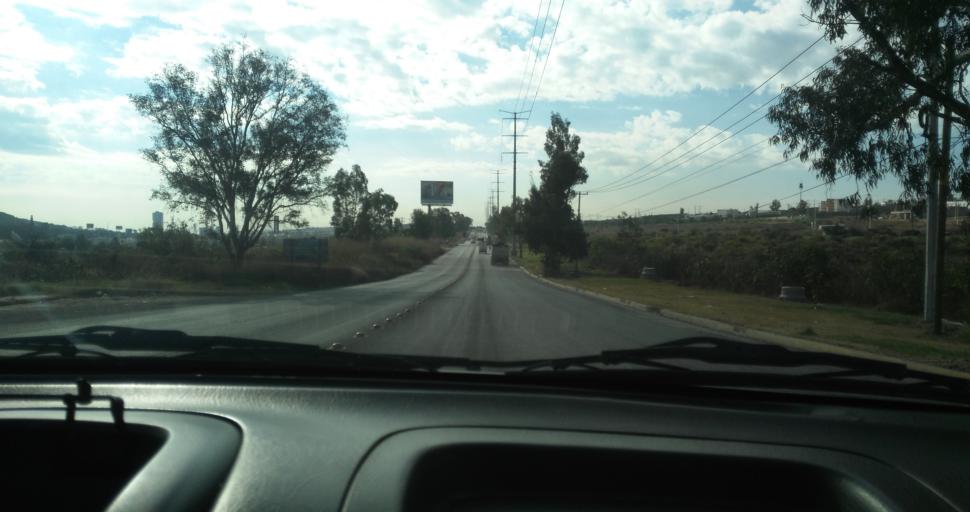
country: MX
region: Guanajuato
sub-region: Leon
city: Fraccionamiento Paseo de las Torres
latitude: 21.1737
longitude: -101.7391
